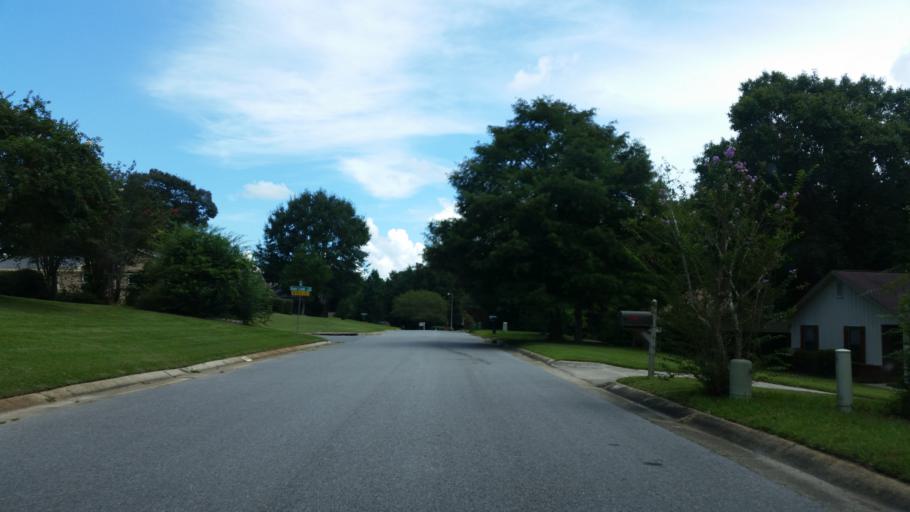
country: US
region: Florida
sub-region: Escambia County
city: Ensley
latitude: 30.5452
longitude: -87.2429
